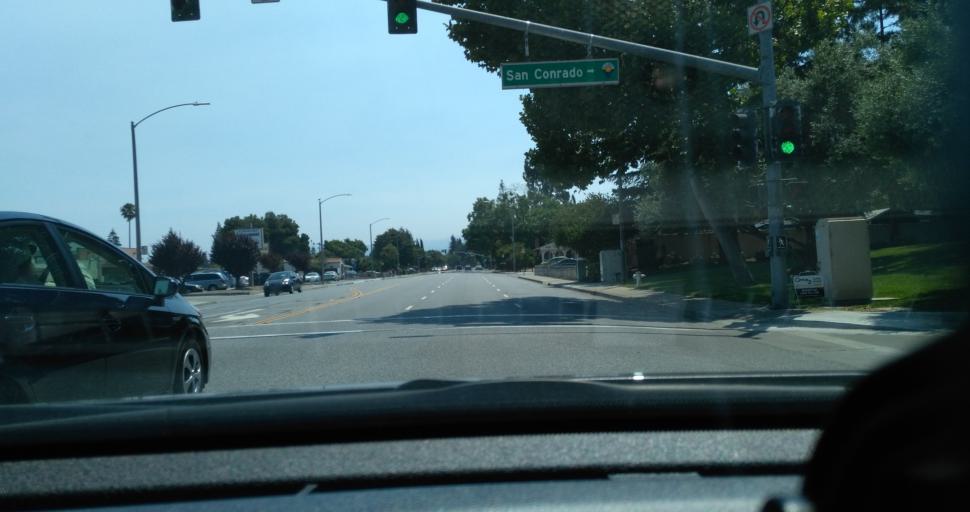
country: US
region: California
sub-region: Santa Clara County
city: Sunnyvale
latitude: 37.3913
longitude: -122.0143
